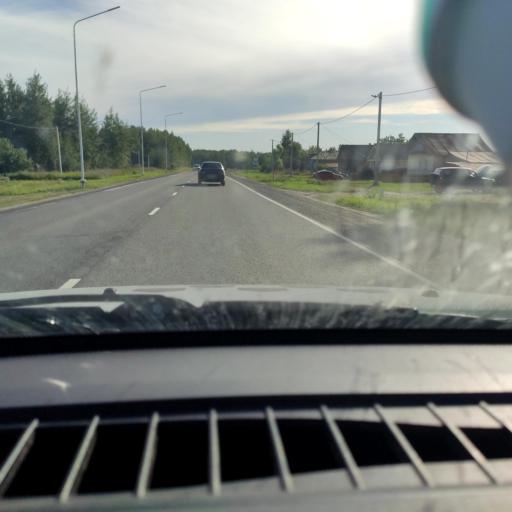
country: RU
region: Kirov
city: Vakhrushi
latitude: 58.6691
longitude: 49.9382
